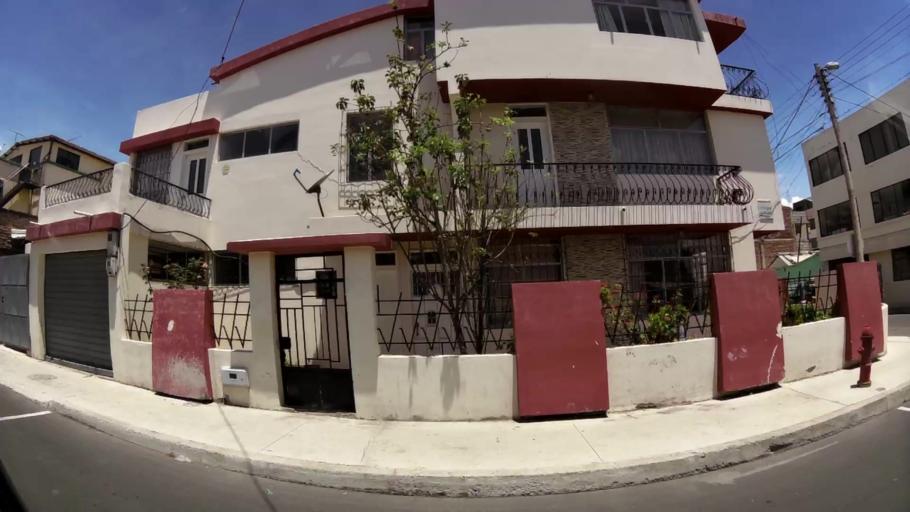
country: EC
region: Chimborazo
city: Riobamba
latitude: -1.6641
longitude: -78.6518
